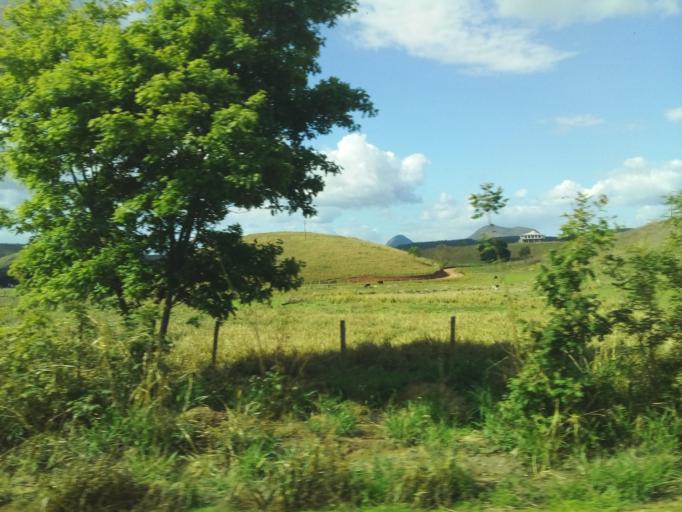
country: BR
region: Minas Gerais
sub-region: Conselheiro Pena
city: Conselheiro Pena
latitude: -18.9821
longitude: -41.6166
